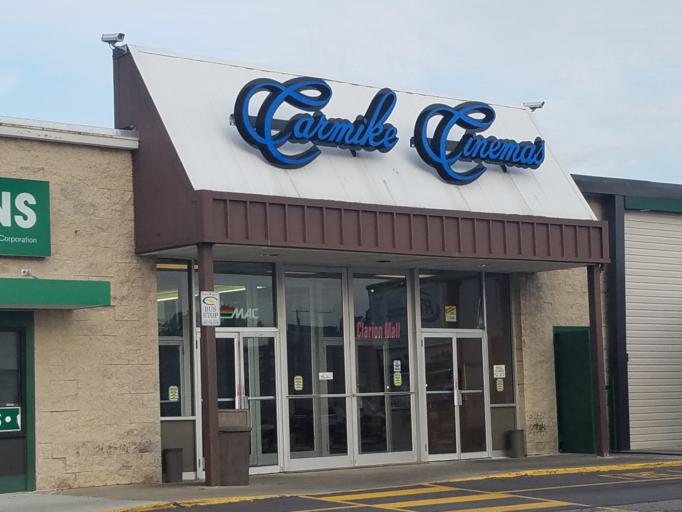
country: US
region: Pennsylvania
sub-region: Clarion County
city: Clarion
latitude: 41.1935
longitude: -79.3946
